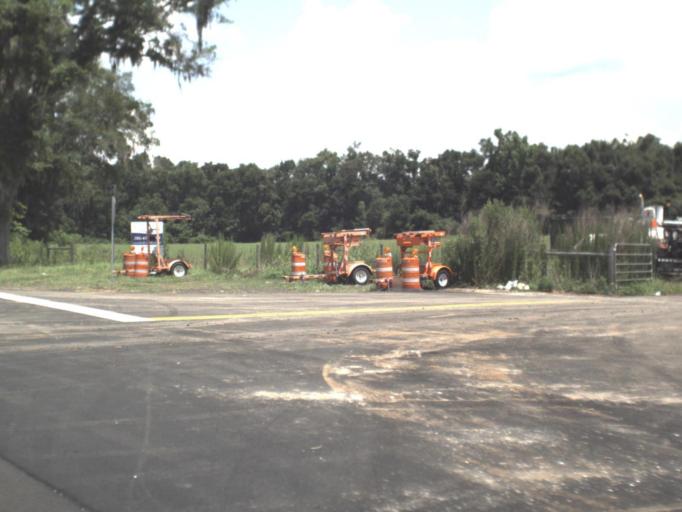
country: US
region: Florida
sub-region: Alachua County
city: Alachua
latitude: 29.7792
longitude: -82.4513
